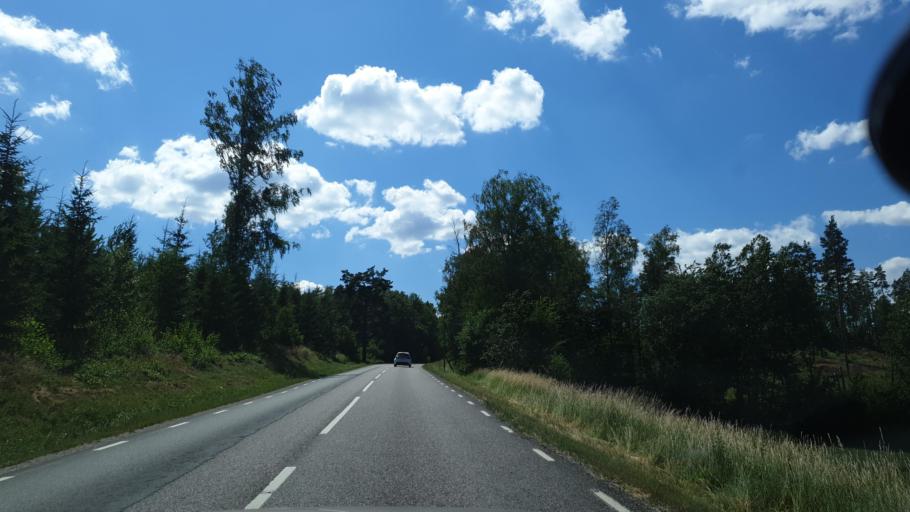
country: SE
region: Stockholm
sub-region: Nykvarns Kommun
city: Nykvarn
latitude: 59.2413
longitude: 17.4502
